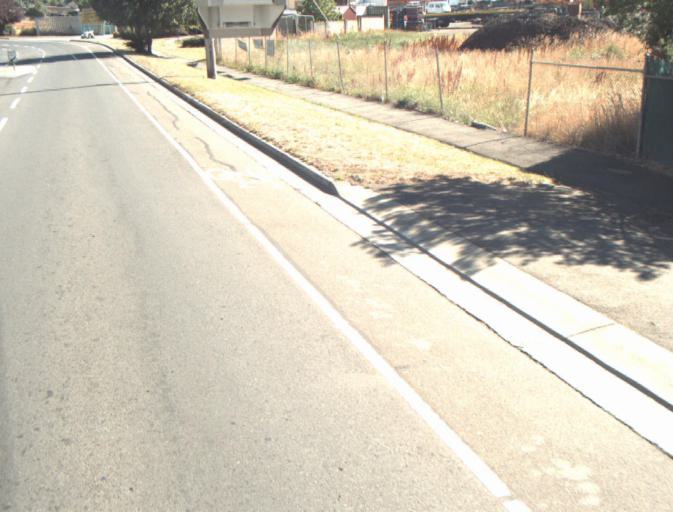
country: AU
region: Tasmania
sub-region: Launceston
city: Mayfield
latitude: -41.3821
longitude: 147.1286
